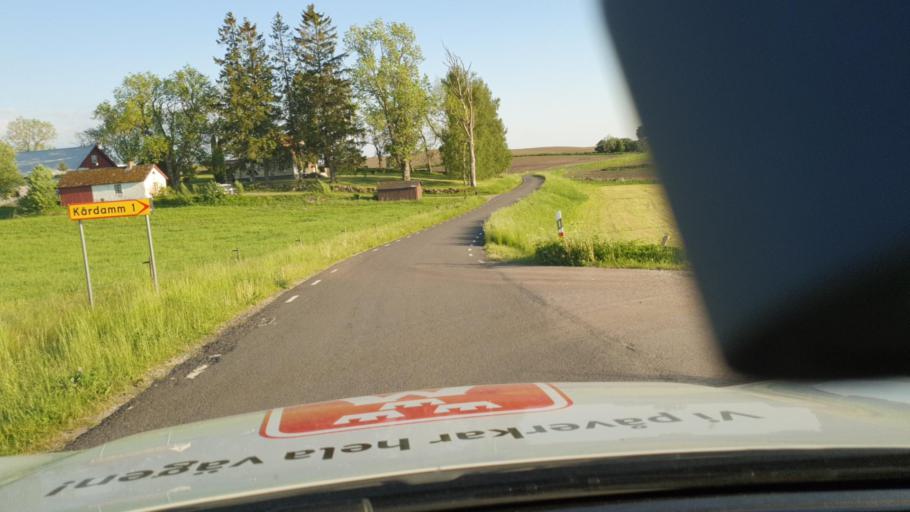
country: SE
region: Vaestra Goetaland
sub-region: Falkopings Kommun
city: Akarp
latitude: 58.1006
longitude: 13.6912
